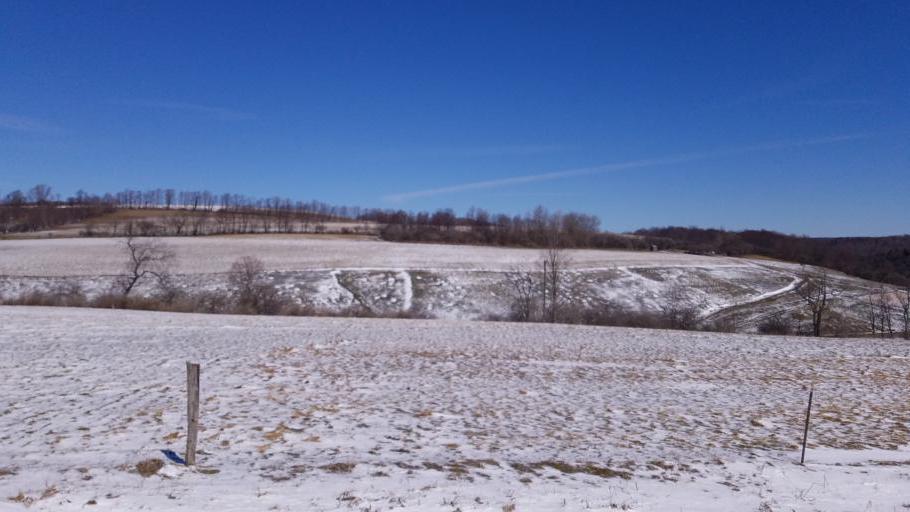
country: US
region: New York
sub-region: Allegany County
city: Andover
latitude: 42.0083
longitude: -77.7662
